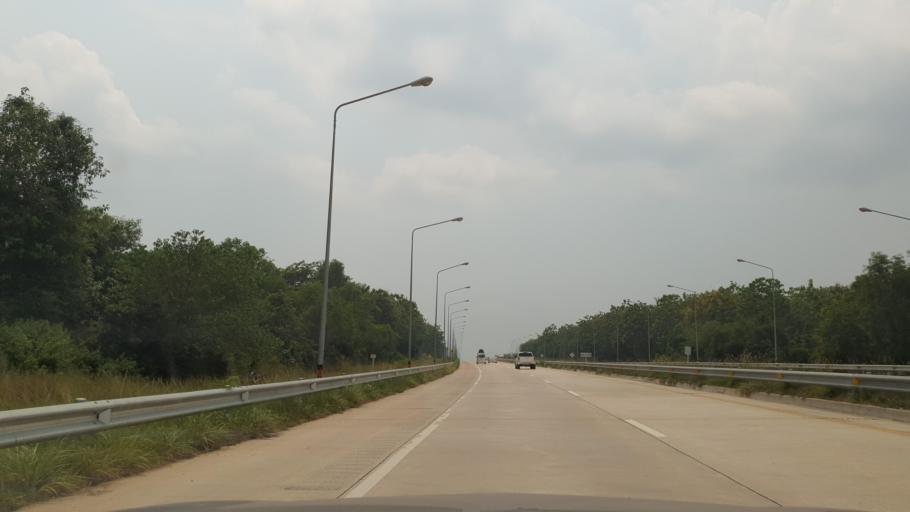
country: TH
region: Chon Buri
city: Phatthaya
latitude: 12.8401
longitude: 100.9546
